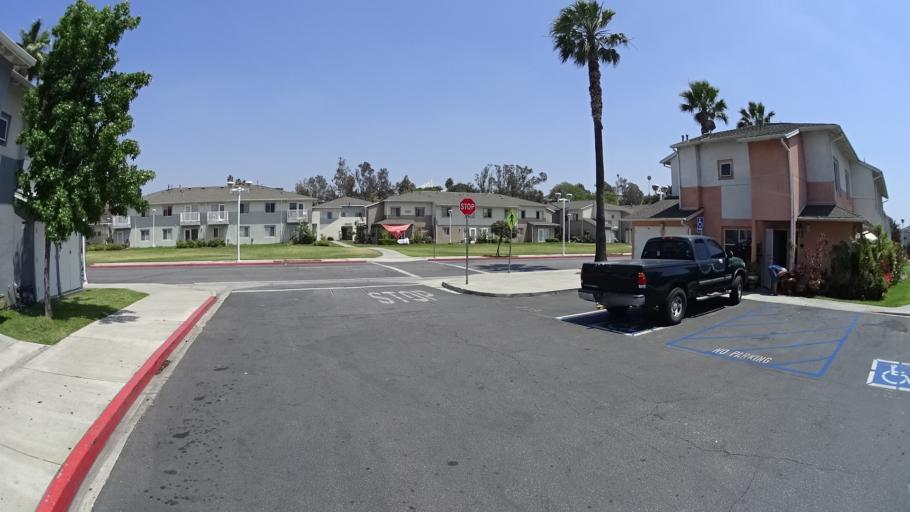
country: US
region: California
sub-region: Los Angeles County
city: Boyle Heights
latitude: 34.0418
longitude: -118.2229
